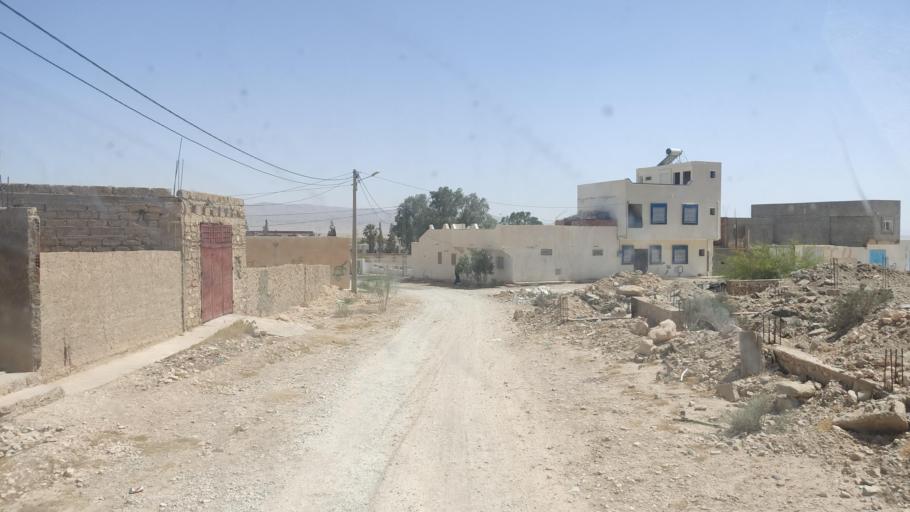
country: TN
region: Gafsa
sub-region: Gafsa Municipality
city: Gafsa
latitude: 34.3420
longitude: 8.9381
